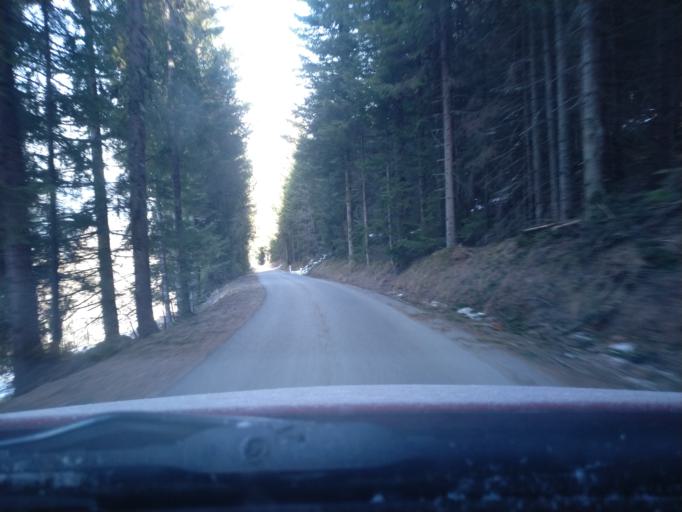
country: AT
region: Carinthia
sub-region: Politischer Bezirk Villach Land
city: Arriach
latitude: 46.7089
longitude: 13.8942
